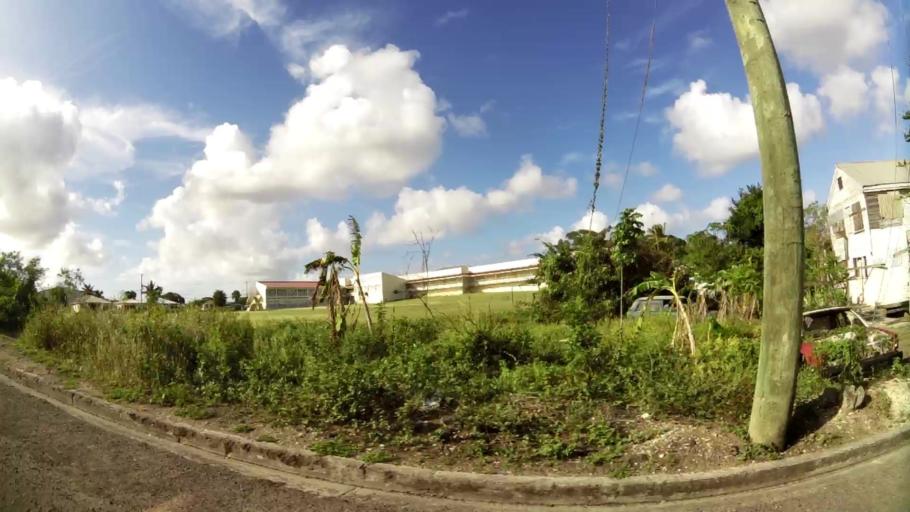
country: AG
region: Saint Peter
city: All Saints
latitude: 17.0506
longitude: -61.7999
